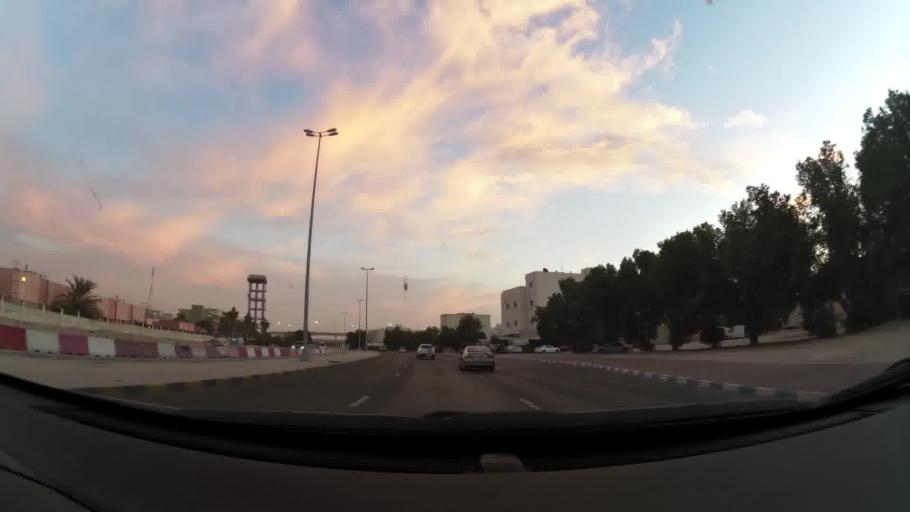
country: KW
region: Al Asimah
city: Ar Rabiyah
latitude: 29.3162
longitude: 47.8823
